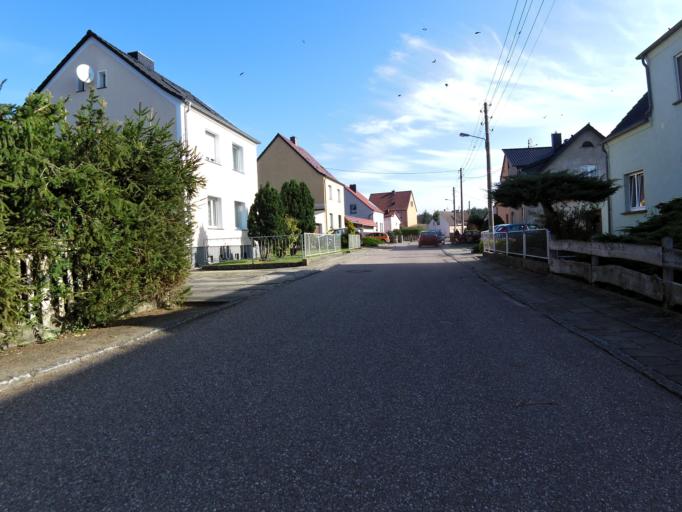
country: DE
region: Saxony-Anhalt
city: Coswig
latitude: 51.8733
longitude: 12.4738
